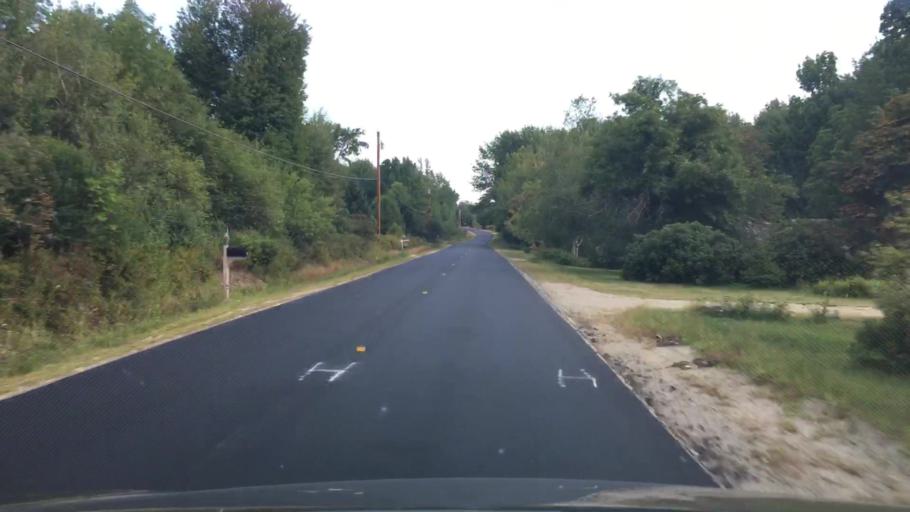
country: US
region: Maine
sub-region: Hancock County
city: Orland
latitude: 44.5515
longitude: -68.6212
